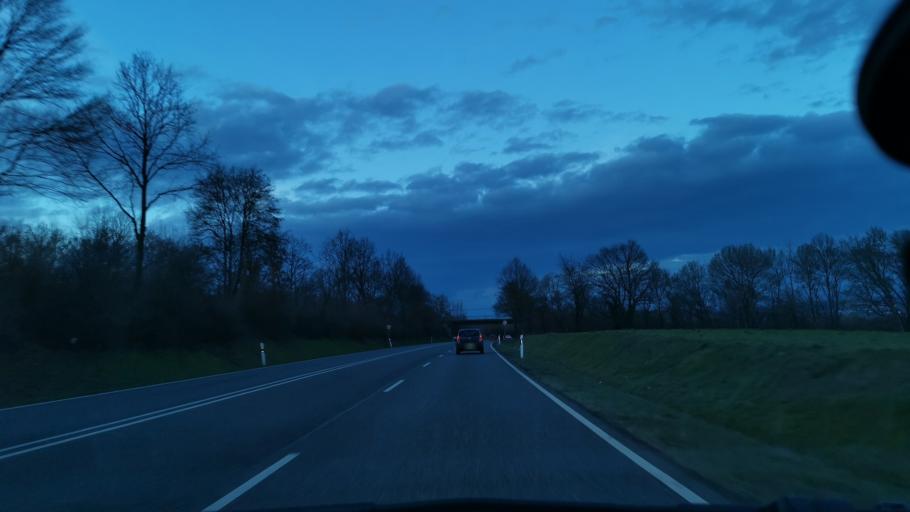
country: DE
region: Hesse
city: Breitenbach
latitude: 50.9394
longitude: 9.7710
